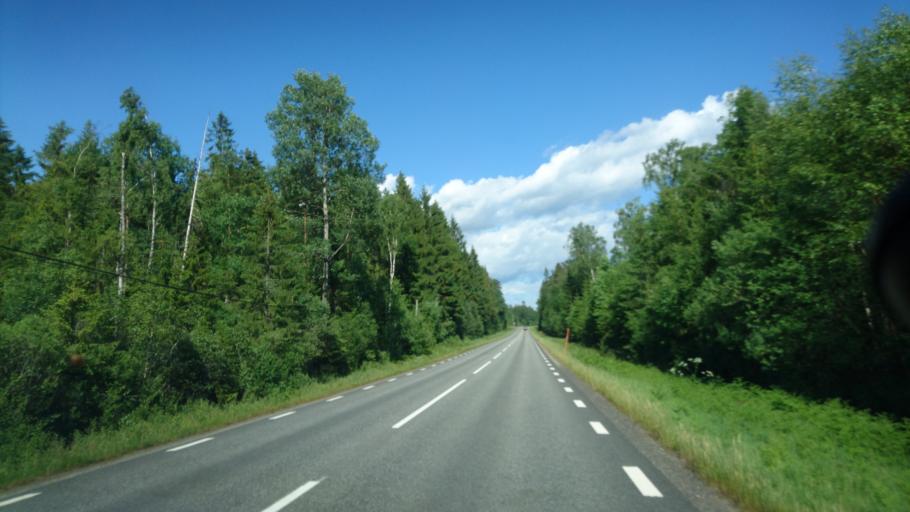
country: SE
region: Kronoberg
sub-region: Almhults Kommun
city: AElmhult
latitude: 56.4831
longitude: 14.1720
